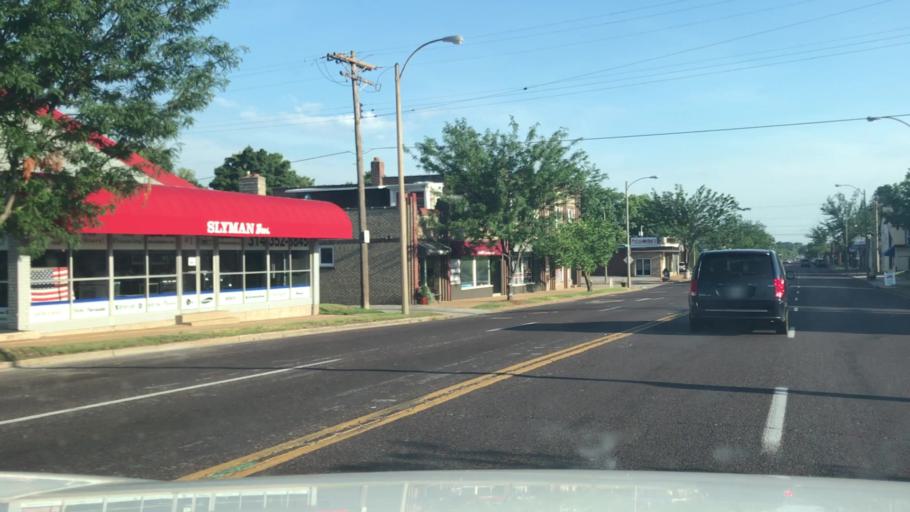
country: US
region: Missouri
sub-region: Saint Louis County
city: Maplewood
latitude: 38.5867
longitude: -90.2925
